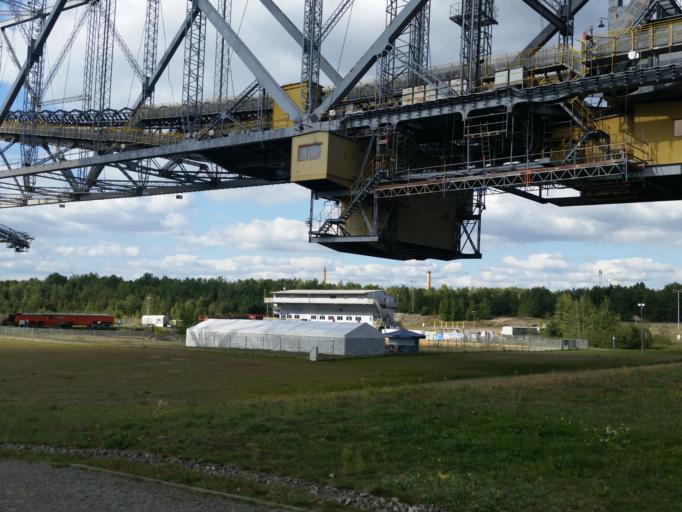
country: DE
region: Brandenburg
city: Sallgast
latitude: 51.5863
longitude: 13.7807
